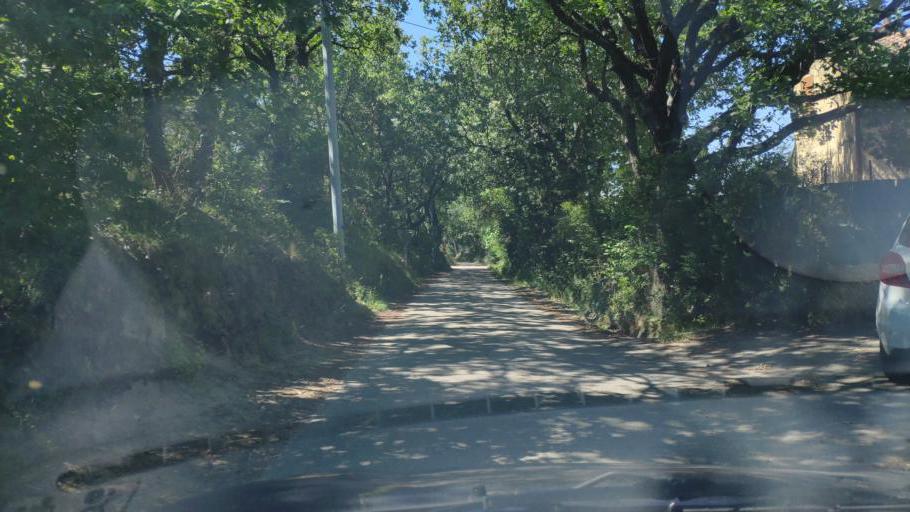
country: FR
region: Provence-Alpes-Cote d'Azur
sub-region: Departement du Vaucluse
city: Loriol-du-Comtat
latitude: 44.0740
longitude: 5.0133
